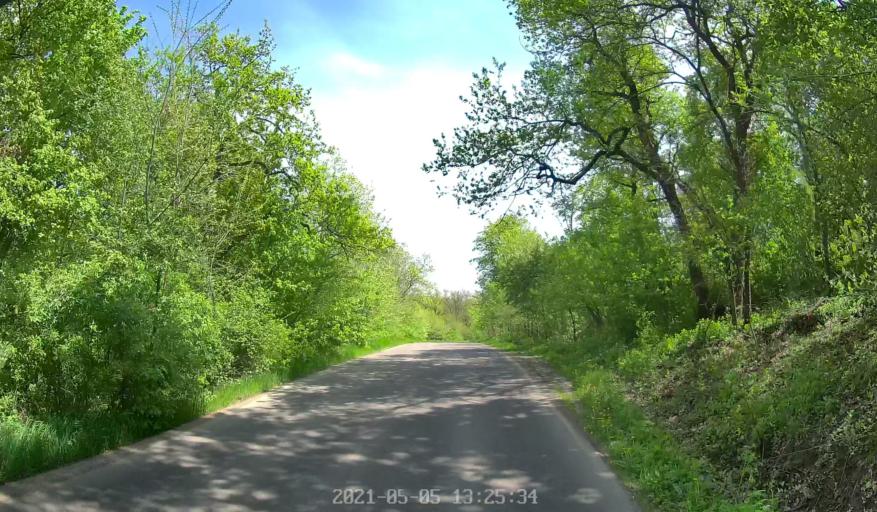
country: MD
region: Chisinau
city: Vadul lui Voda
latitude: 47.0718
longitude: 29.1135
